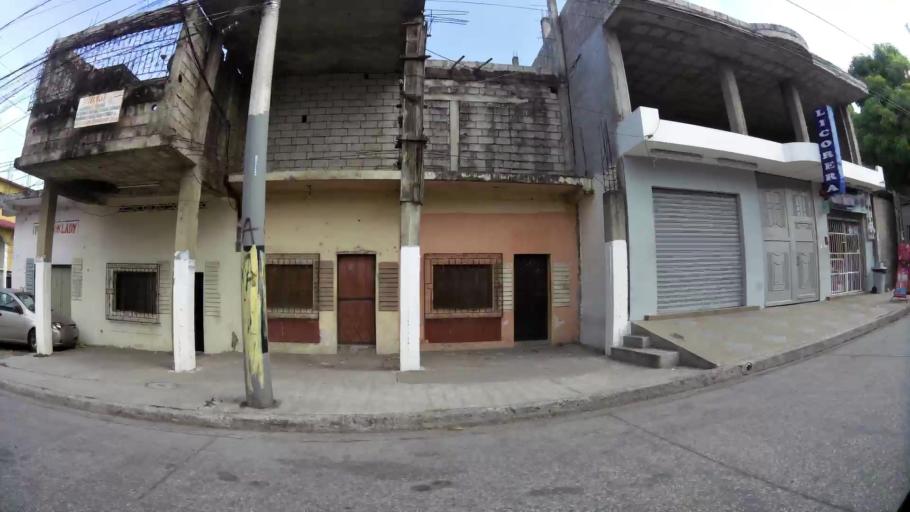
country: EC
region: Guayas
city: Guayaquil
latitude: -2.1413
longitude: -79.9395
